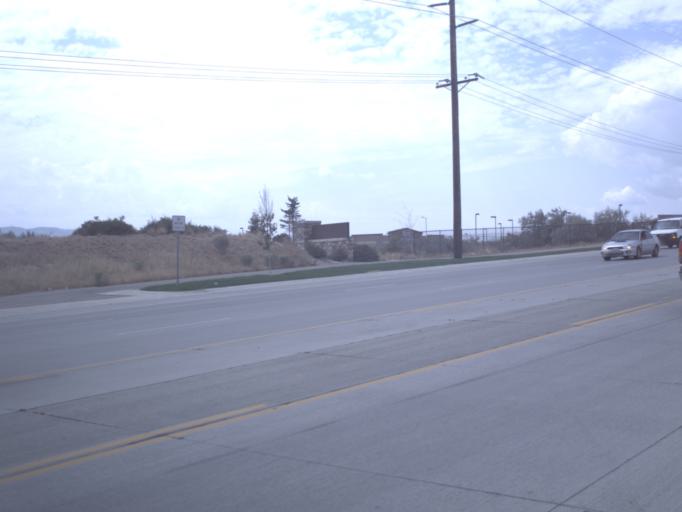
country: US
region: Utah
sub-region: Utah County
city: Alpine
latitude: 40.4318
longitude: -111.8197
